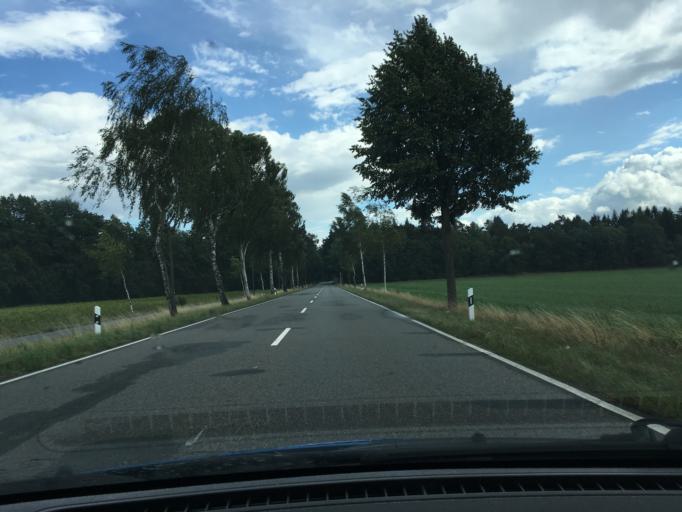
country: DE
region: Lower Saxony
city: Wietzendorf
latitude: 52.9827
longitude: 9.9414
